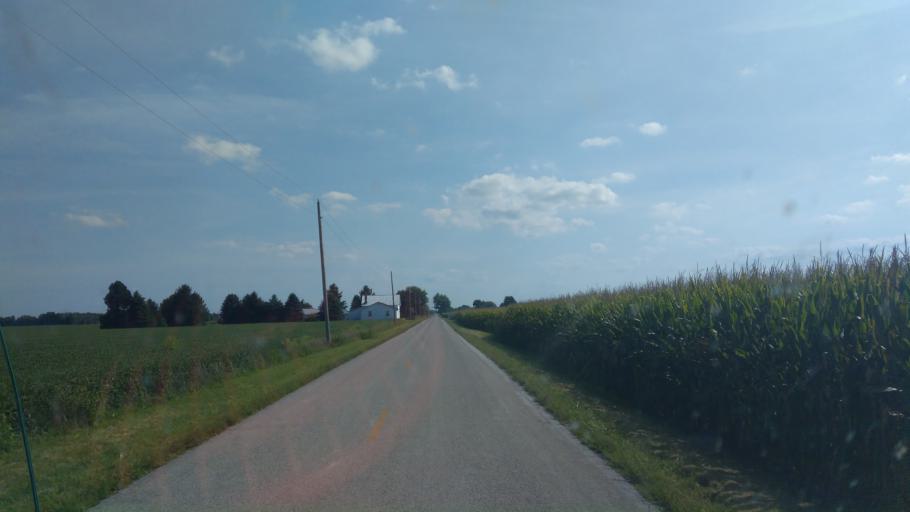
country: US
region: Ohio
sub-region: Hardin County
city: Forest
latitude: 40.7180
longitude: -83.5145
